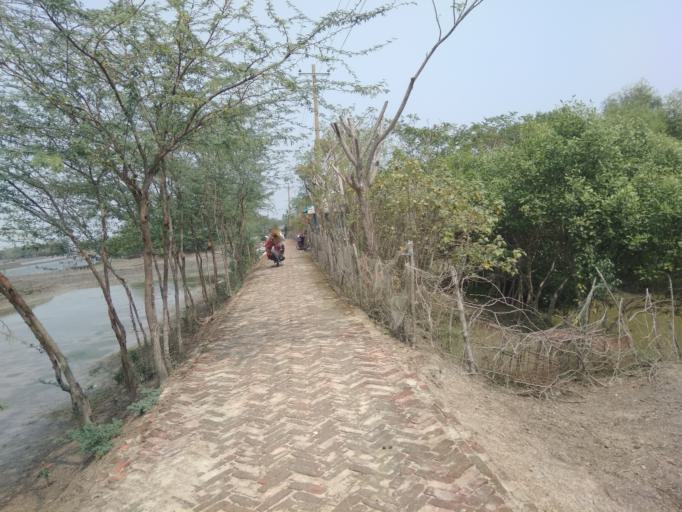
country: IN
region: West Bengal
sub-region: North 24 Parganas
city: Taki
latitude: 22.2775
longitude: 89.2844
